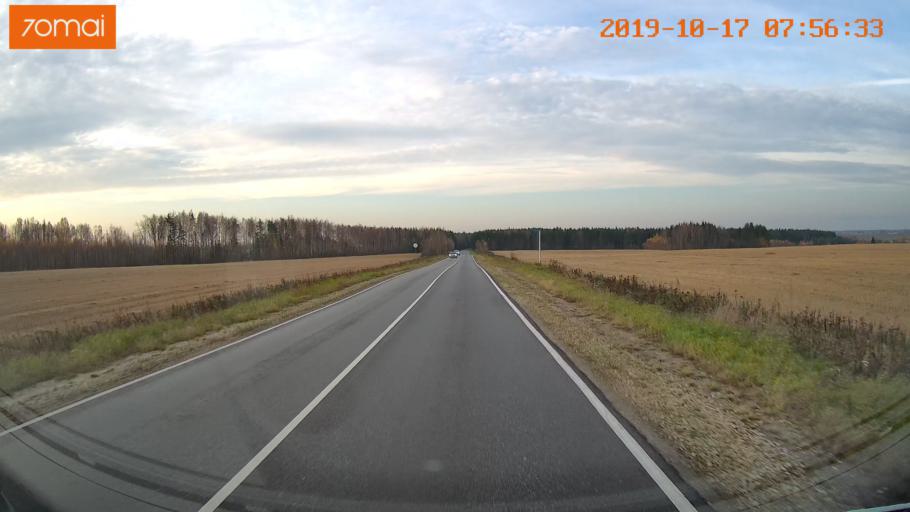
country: RU
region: Vladimir
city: Bavleny
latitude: 56.4217
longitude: 39.5891
